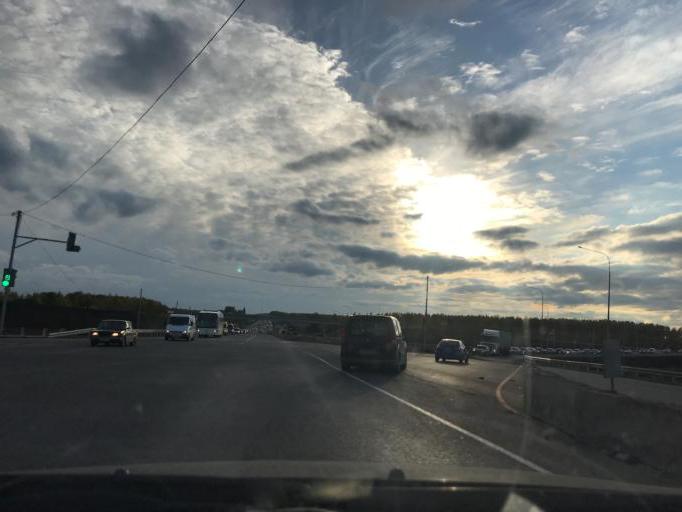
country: RU
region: Kaluga
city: Kurovskoye
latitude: 54.5286
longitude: 35.9873
